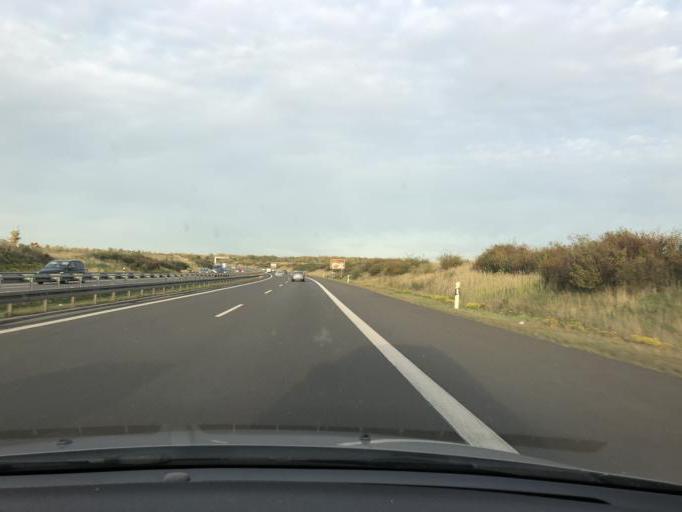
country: DE
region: Saxony
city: Rotha
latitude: 51.2497
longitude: 12.4254
